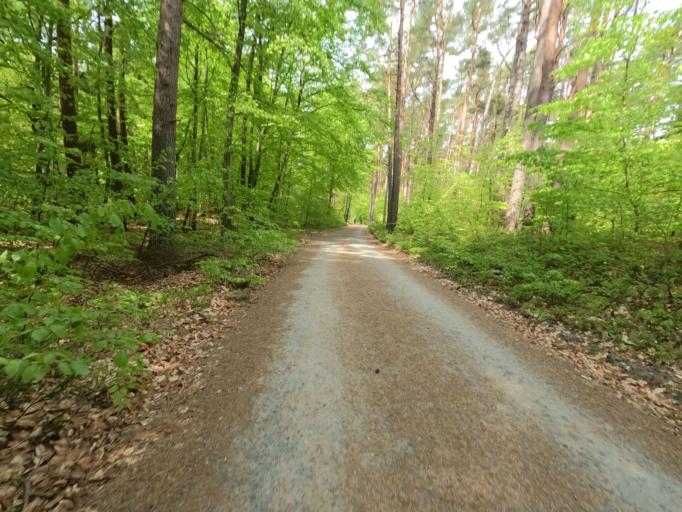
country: DE
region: Mecklenburg-Vorpommern
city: Ostseebad Prerow
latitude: 54.4473
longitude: 12.5323
